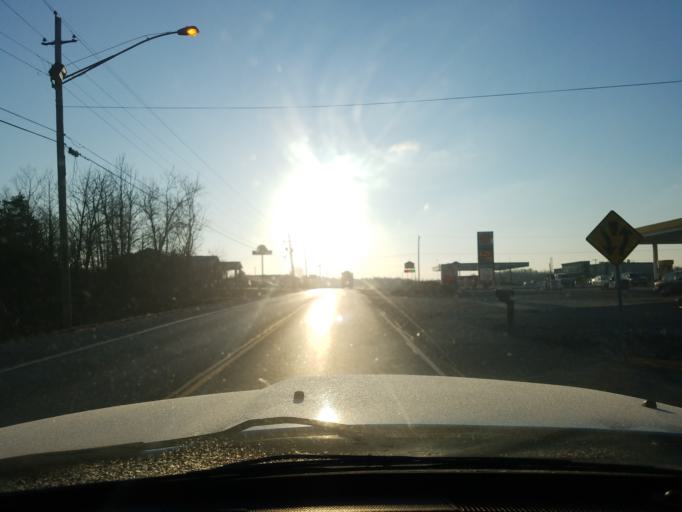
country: US
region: Kentucky
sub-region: Muhlenberg County
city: Central City
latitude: 37.2859
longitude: -87.1152
